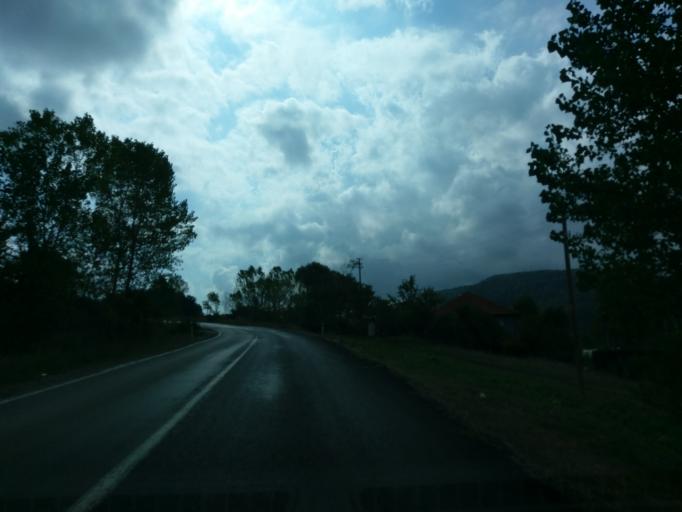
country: TR
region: Sinop
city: Erfelek
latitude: 41.9464
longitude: 34.7760
